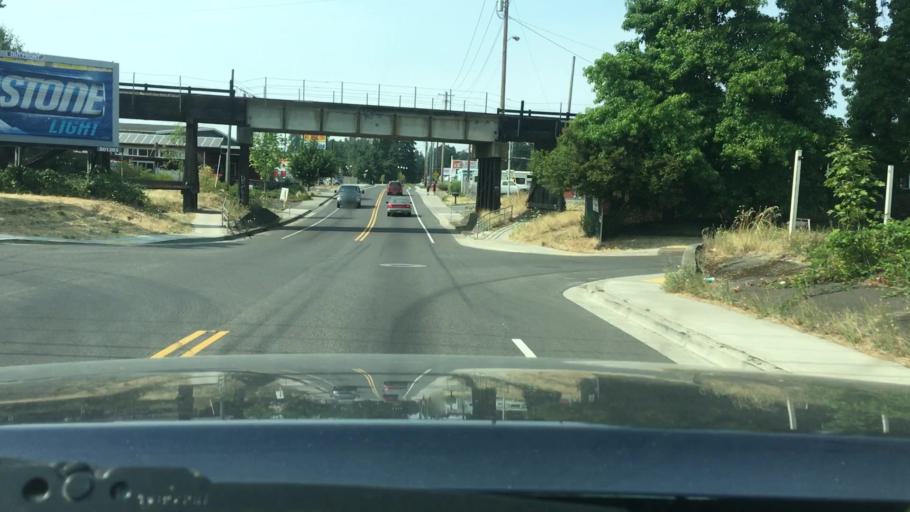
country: US
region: Oregon
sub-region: Lane County
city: Springfield
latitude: 44.0415
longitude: -123.0292
